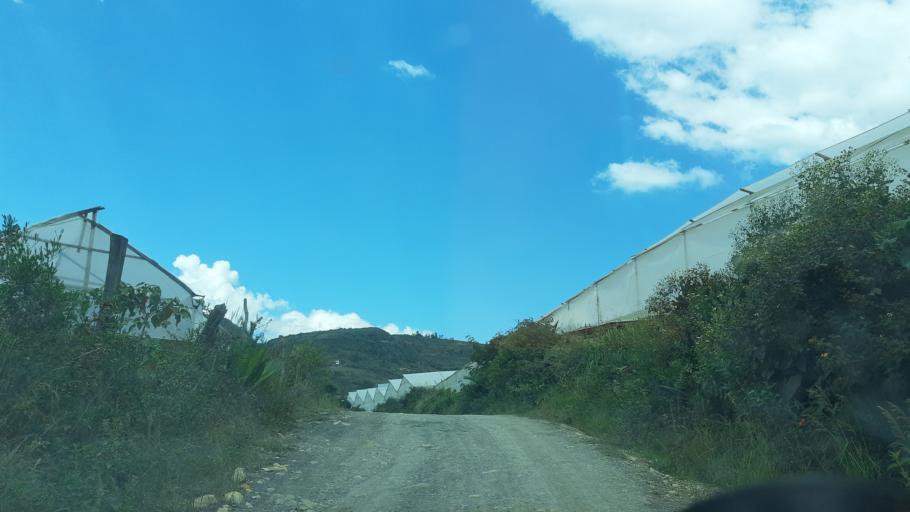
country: CO
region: Boyaca
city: Santa Sofia
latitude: 5.6898
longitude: -73.5701
